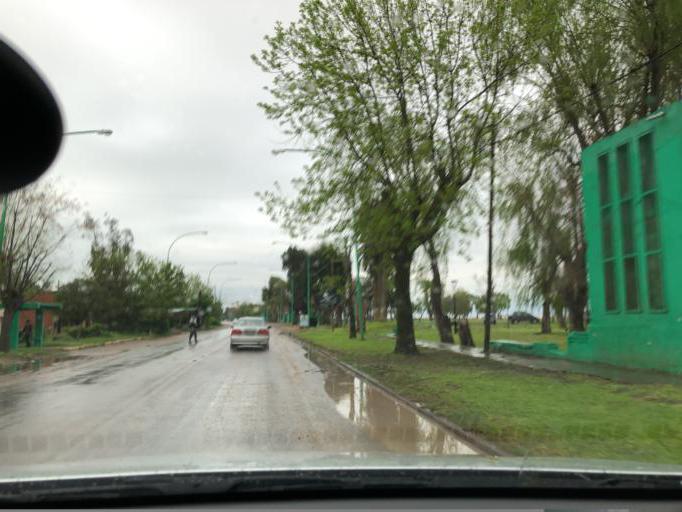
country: AR
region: Buenos Aires
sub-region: Partido de Ensenada
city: Ensenada
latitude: -34.8286
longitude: -57.9566
